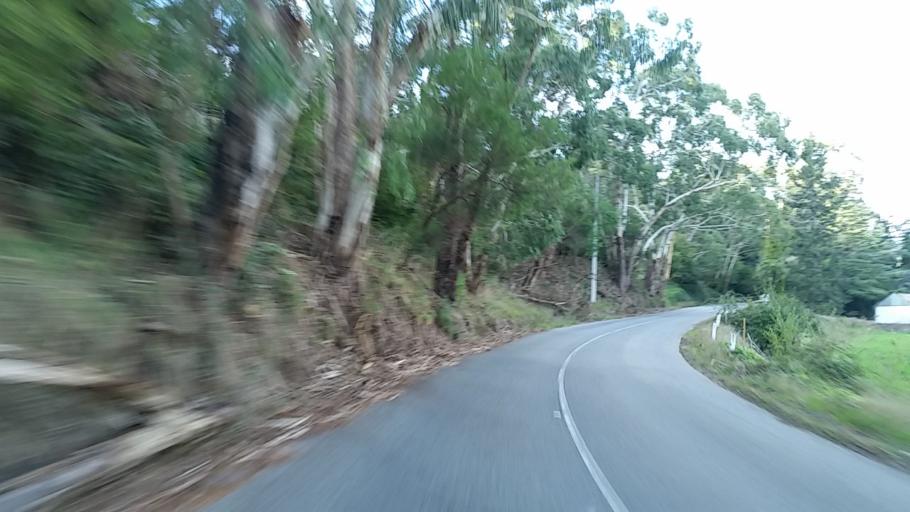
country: AU
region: South Australia
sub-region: Adelaide Hills
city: Adelaide Hills
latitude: -34.8915
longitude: 138.7365
